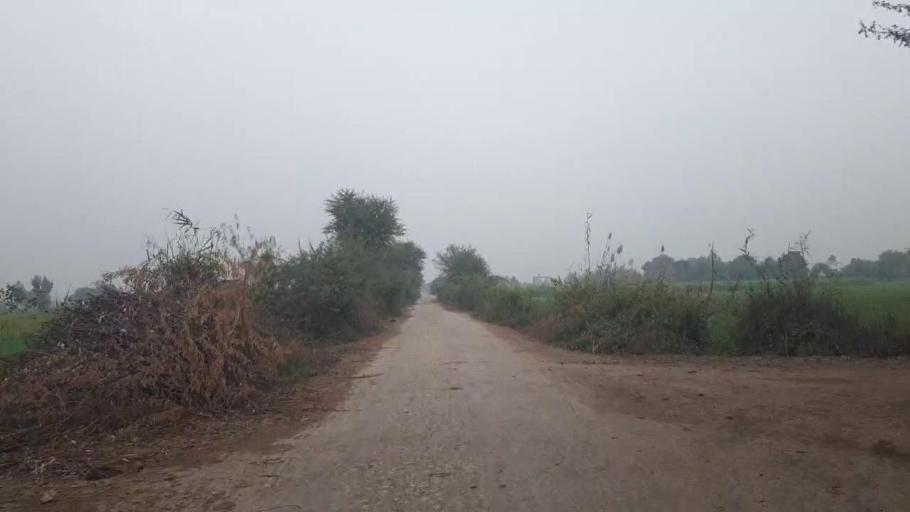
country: PK
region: Sindh
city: Tando Adam
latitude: 25.7519
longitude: 68.7024
